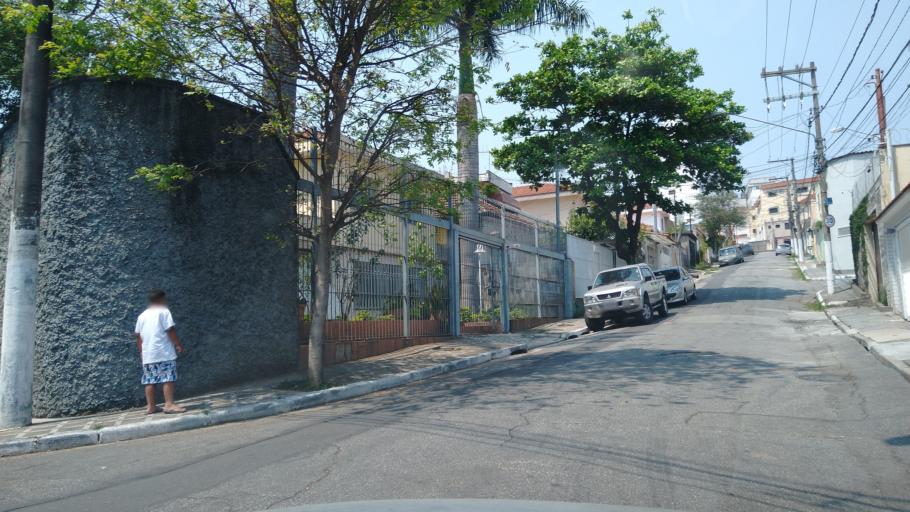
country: BR
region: Sao Paulo
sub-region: Sao Paulo
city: Sao Paulo
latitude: -23.4982
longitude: -46.6054
